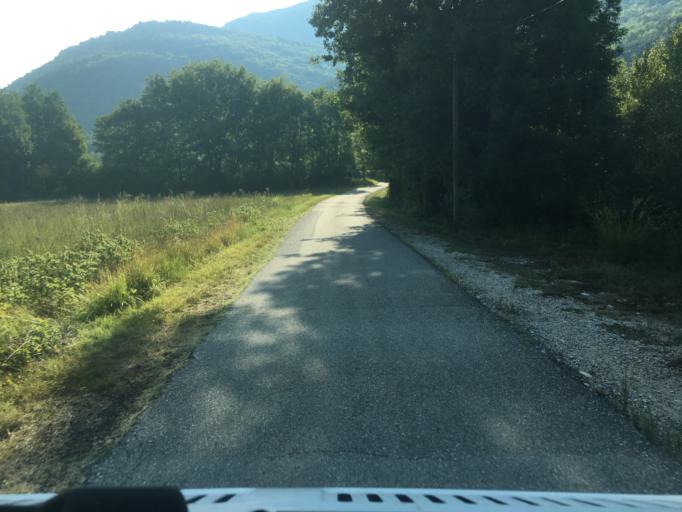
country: FR
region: Provence-Alpes-Cote d'Azur
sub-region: Departement des Alpes-de-Haute-Provence
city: Mallemoisson
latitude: 43.9394
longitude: 6.1953
